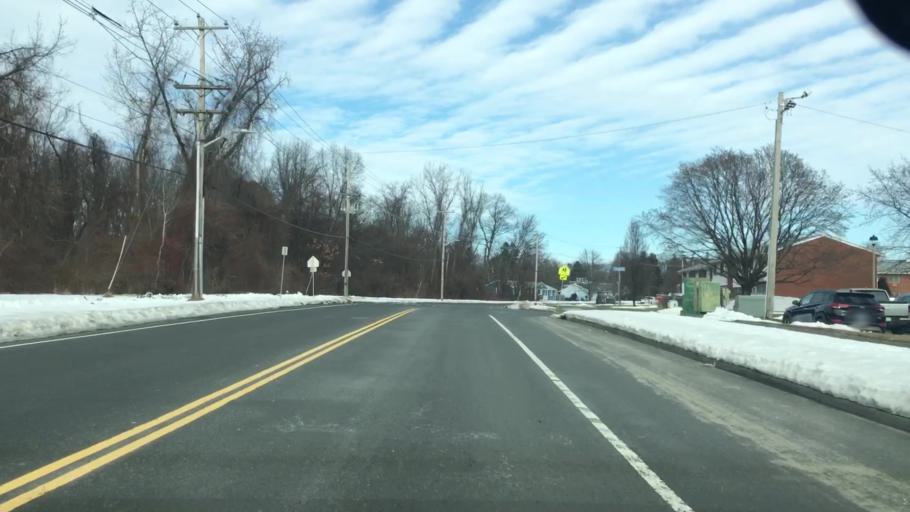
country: US
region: Massachusetts
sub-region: Hampden County
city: Holyoke
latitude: 42.1780
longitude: -72.6404
